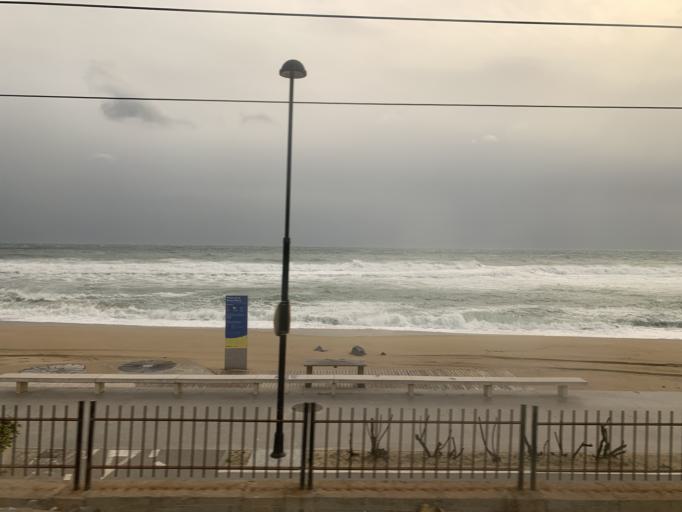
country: ES
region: Catalonia
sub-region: Provincia de Barcelona
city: Montgat
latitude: 41.4588
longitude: 2.2654
